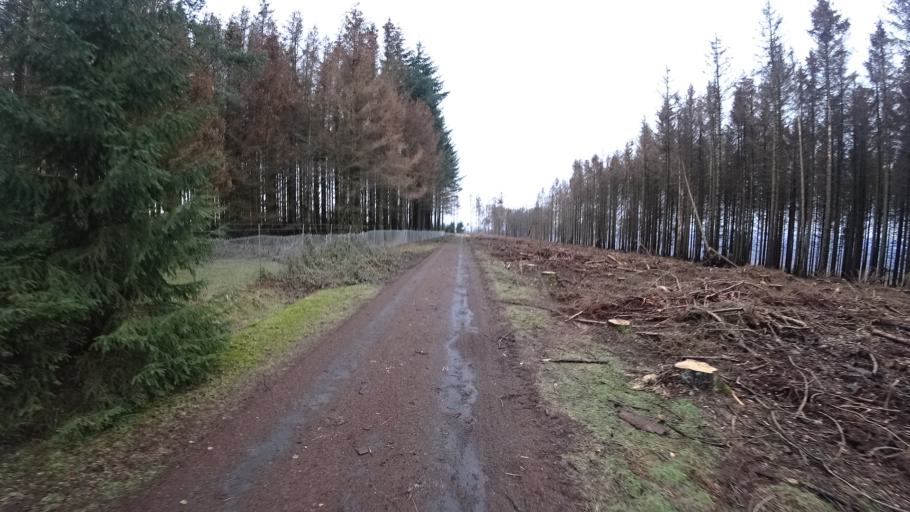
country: DE
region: Rheinland-Pfalz
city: Ransbach-Baumbach
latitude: 50.4247
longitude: 7.7322
